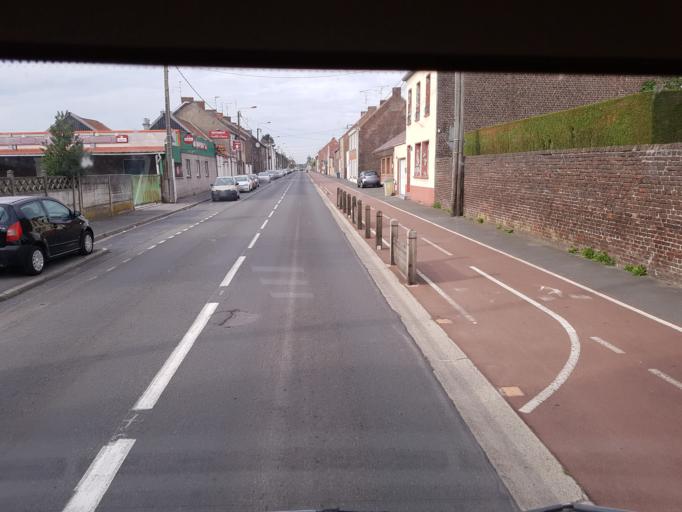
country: FR
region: Nord-Pas-de-Calais
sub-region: Departement du Nord
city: Vieux-Conde
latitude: 50.4640
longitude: 3.5698
